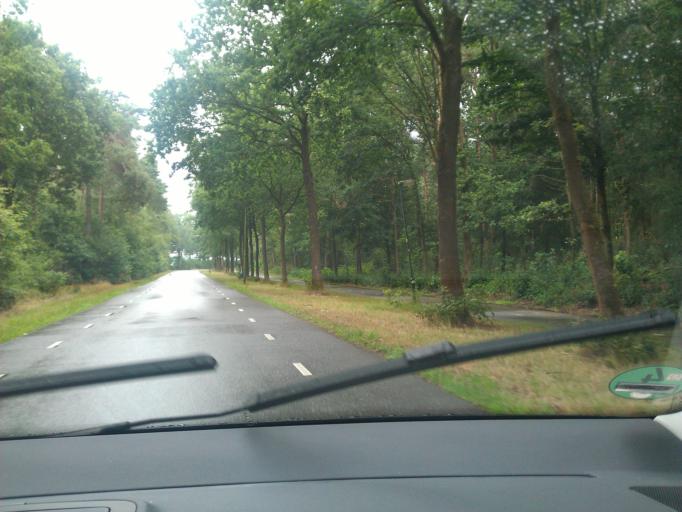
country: NL
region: North Brabant
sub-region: Gemeente Bladel en Netersel
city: Bladel
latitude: 51.3428
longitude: 5.2420
